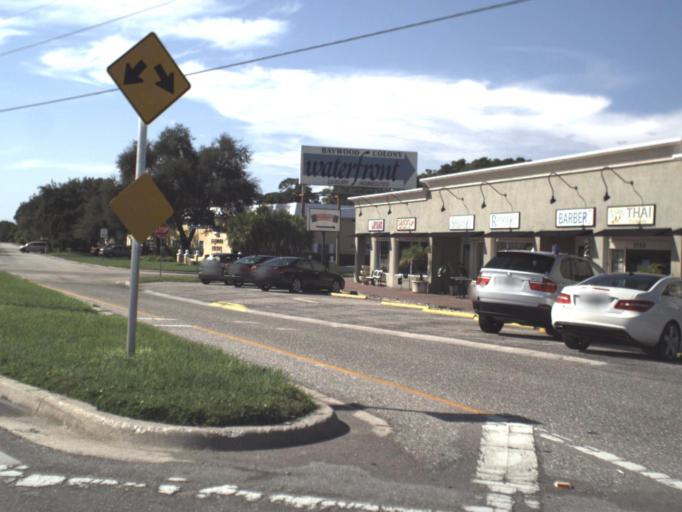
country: US
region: Florida
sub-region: Sarasota County
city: South Sarasota
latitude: 27.2694
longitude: -82.5306
